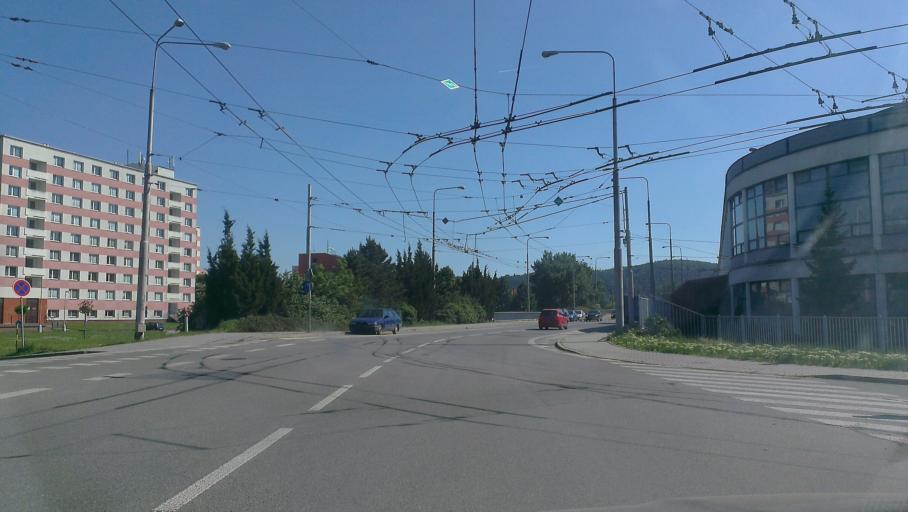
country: CZ
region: South Moravian
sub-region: Mesto Brno
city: Brno
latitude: 49.2163
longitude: 16.5601
